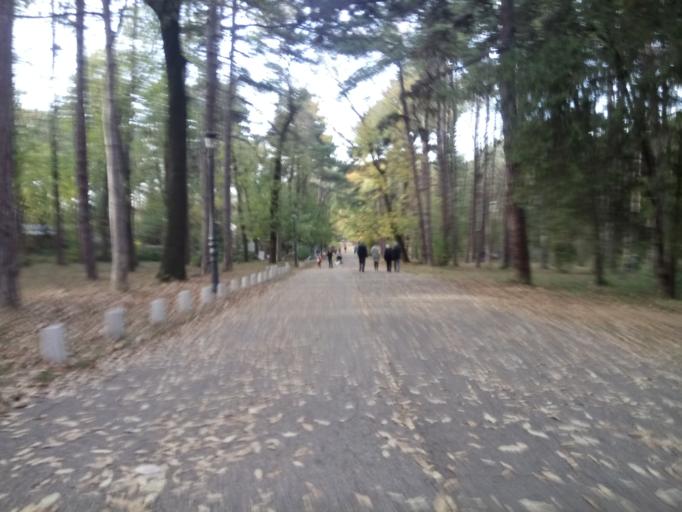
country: BG
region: Sofia-Capital
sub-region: Stolichna Obshtina
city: Sofia
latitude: 42.6826
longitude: 23.3442
